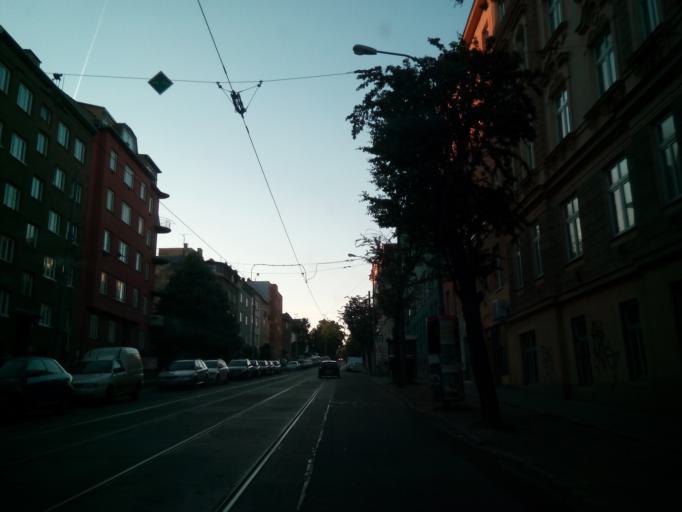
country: CZ
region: South Moravian
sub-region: Mesto Brno
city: Brno
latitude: 49.2051
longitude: 16.6232
